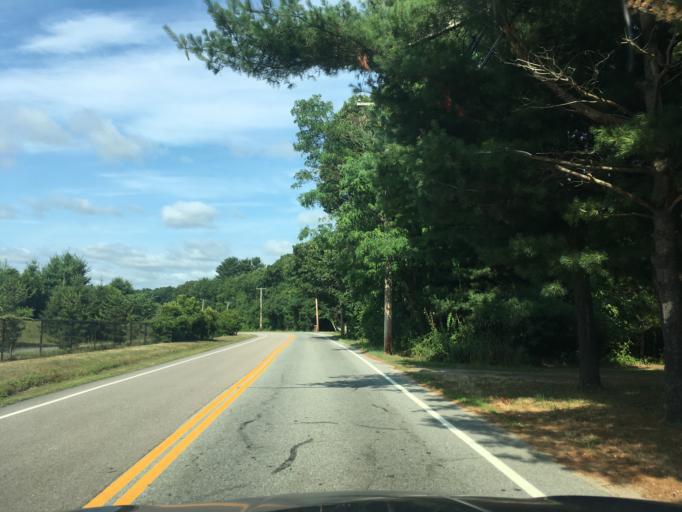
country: US
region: Rhode Island
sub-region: Kent County
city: East Greenwich
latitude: 41.6096
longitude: -71.4418
